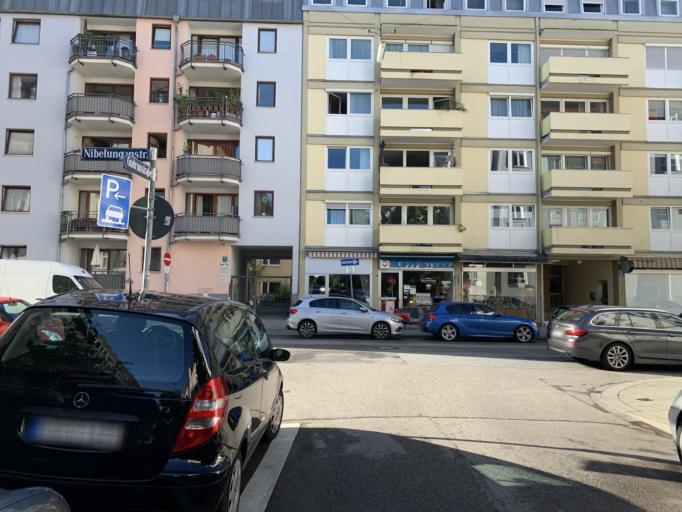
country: DE
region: Bavaria
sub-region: Upper Bavaria
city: Munich
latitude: 48.1532
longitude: 11.5302
